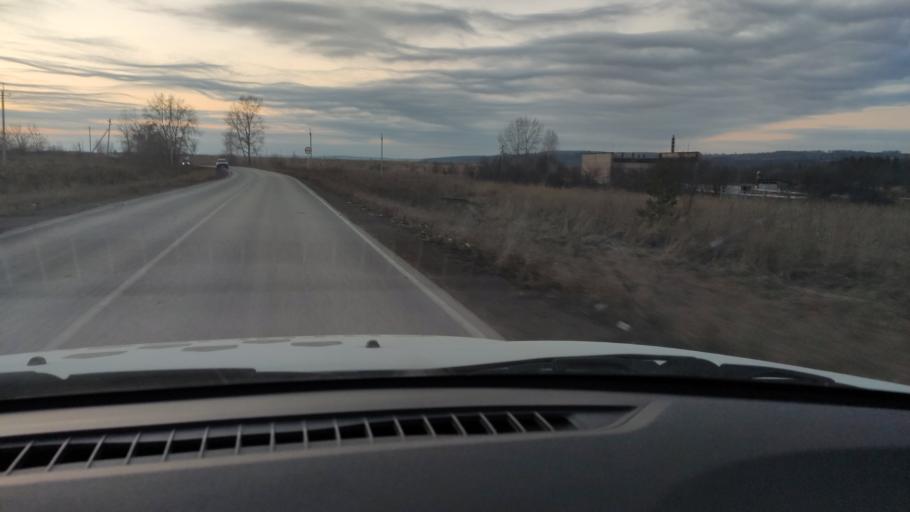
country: RU
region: Perm
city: Lobanovo
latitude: 57.8074
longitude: 56.3514
